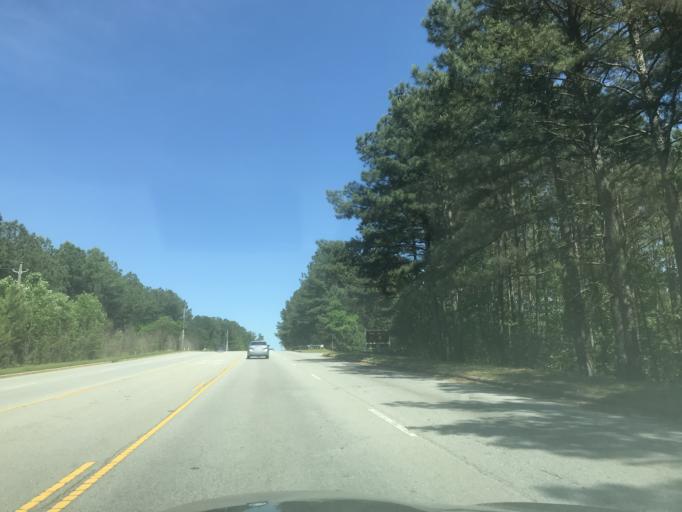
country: US
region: North Carolina
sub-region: Wake County
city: Garner
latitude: 35.7305
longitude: -78.6332
